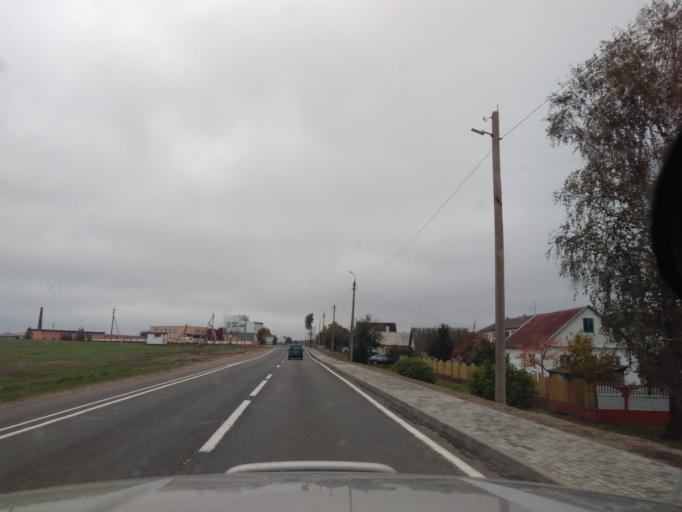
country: BY
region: Minsk
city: Kapyl'
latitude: 53.1395
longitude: 27.0887
